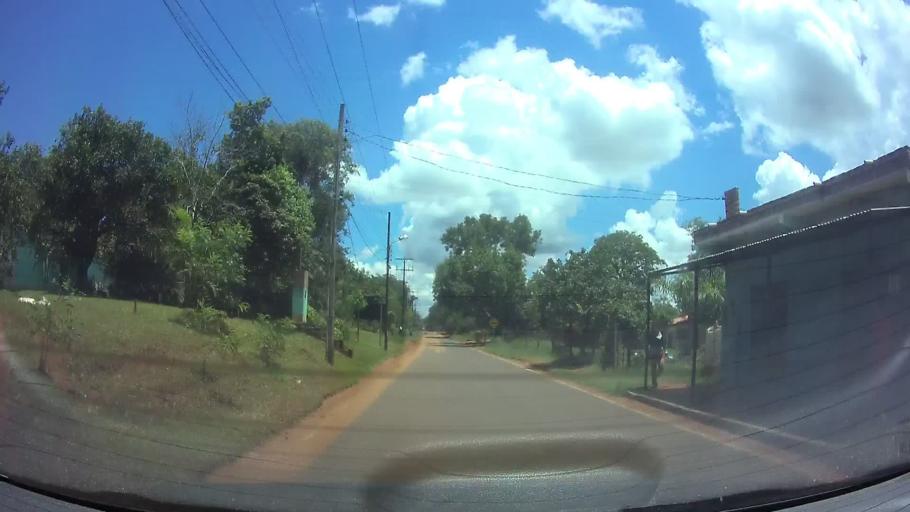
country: PY
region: Central
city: Itaugua
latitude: -25.3786
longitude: -57.3662
